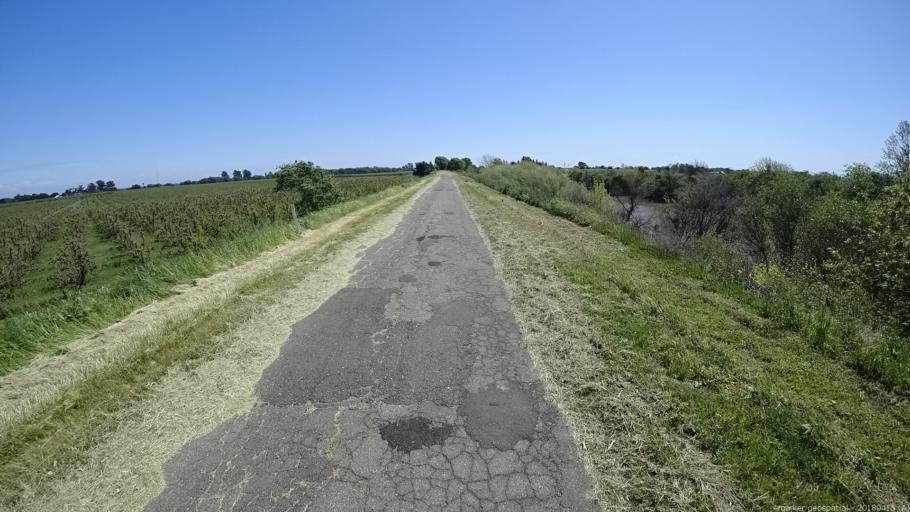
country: US
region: California
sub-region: Sacramento County
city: Walnut Grove
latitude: 38.2842
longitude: -121.6037
